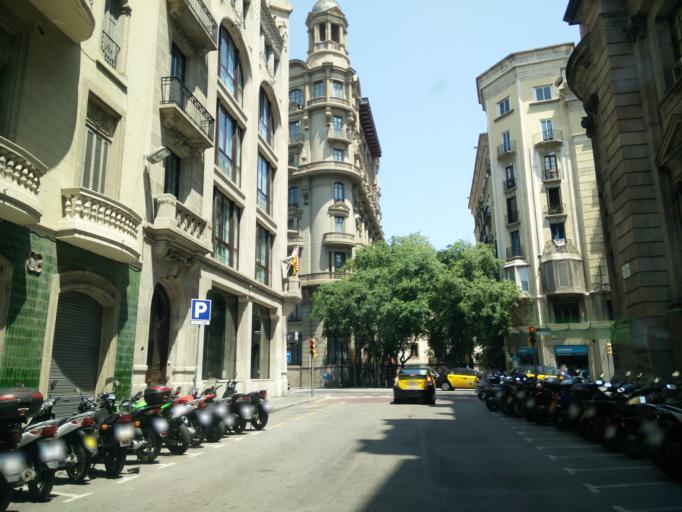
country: ES
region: Catalonia
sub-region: Provincia de Barcelona
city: Ciutat Vella
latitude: 41.3820
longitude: 2.1806
